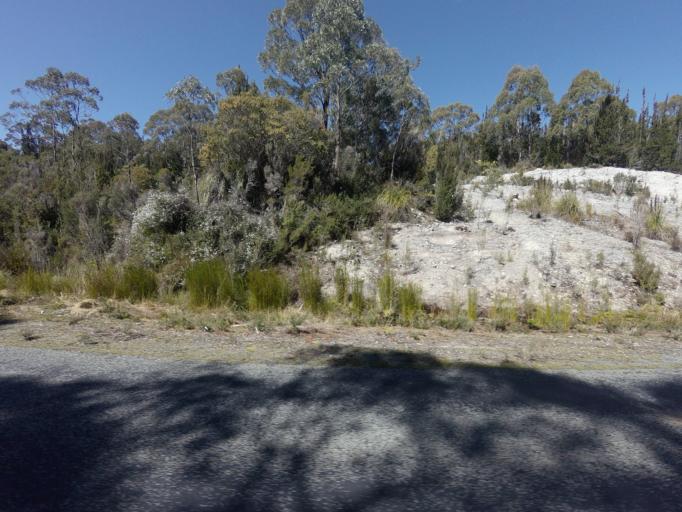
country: AU
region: Tasmania
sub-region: Derwent Valley
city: New Norfolk
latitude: -42.7624
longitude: 146.3966
